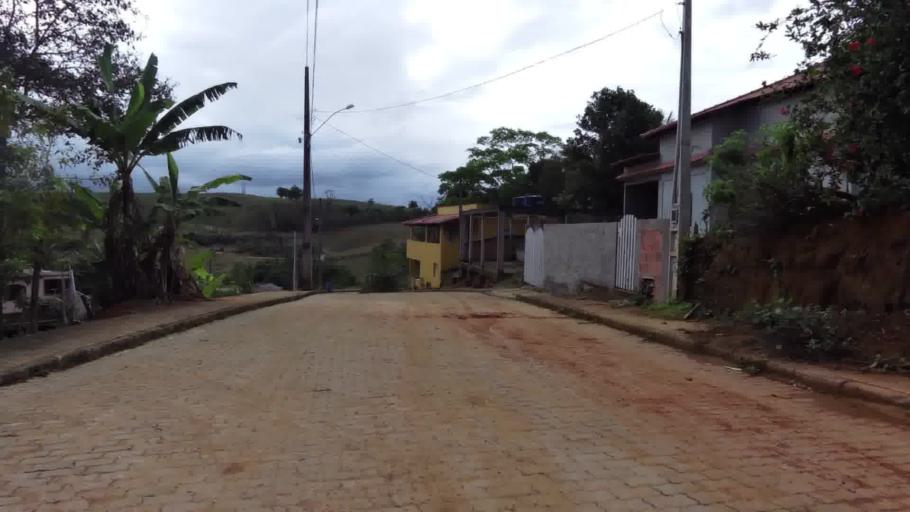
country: BR
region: Espirito Santo
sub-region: Piuma
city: Piuma
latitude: -20.8299
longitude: -40.6992
